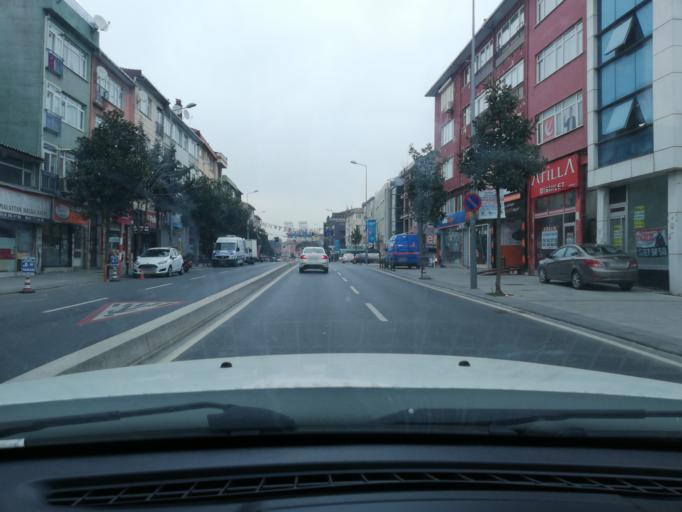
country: TR
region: Istanbul
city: UEskuedar
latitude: 41.0186
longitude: 29.0326
